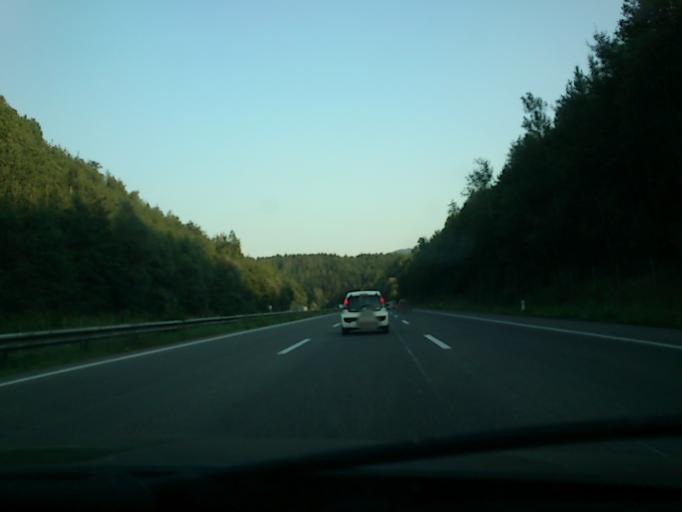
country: AT
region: Styria
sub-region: Politischer Bezirk Graz-Umgebung
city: Gratkorn
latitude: 47.1348
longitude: 15.3563
